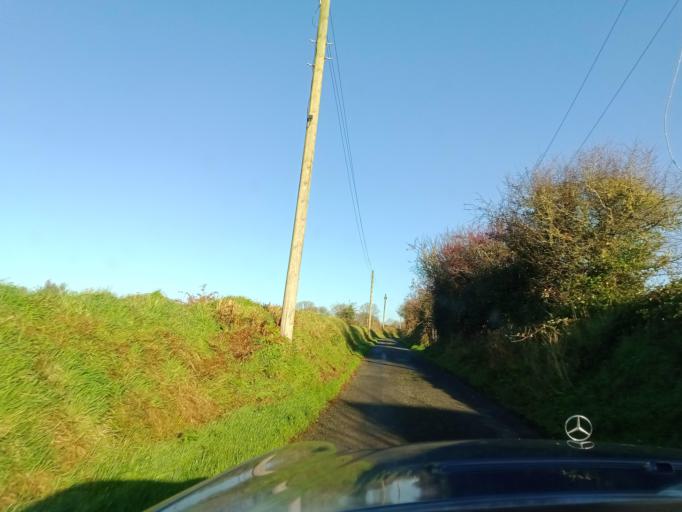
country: IE
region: Leinster
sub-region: Kilkenny
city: Mooncoin
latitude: 52.2964
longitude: -7.2079
